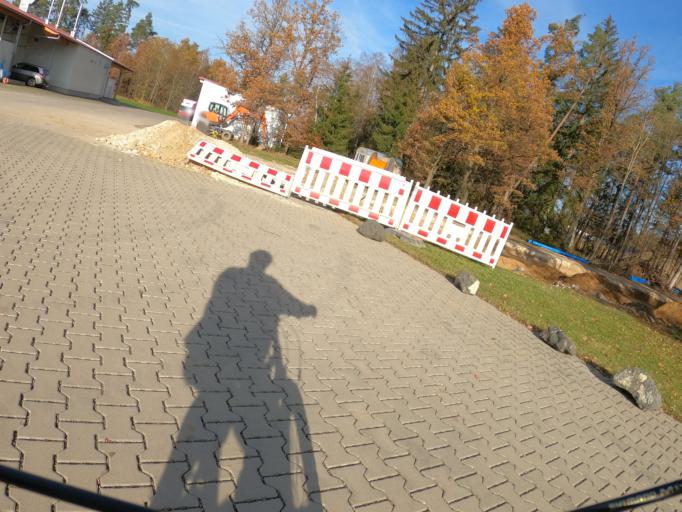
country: DE
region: Bavaria
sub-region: Swabia
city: Nersingen
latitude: 48.4129
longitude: 10.1546
